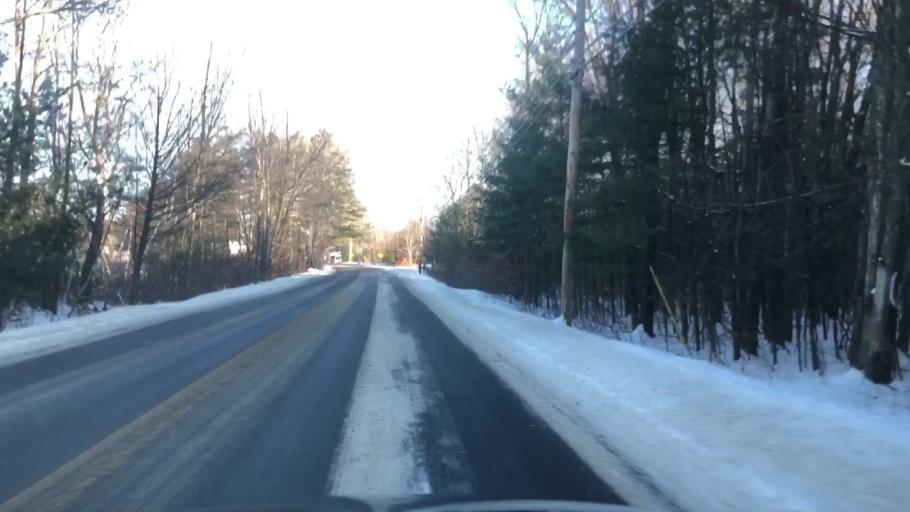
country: US
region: New Hampshire
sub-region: Hillsborough County
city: Milford
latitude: 42.8201
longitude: -71.6684
